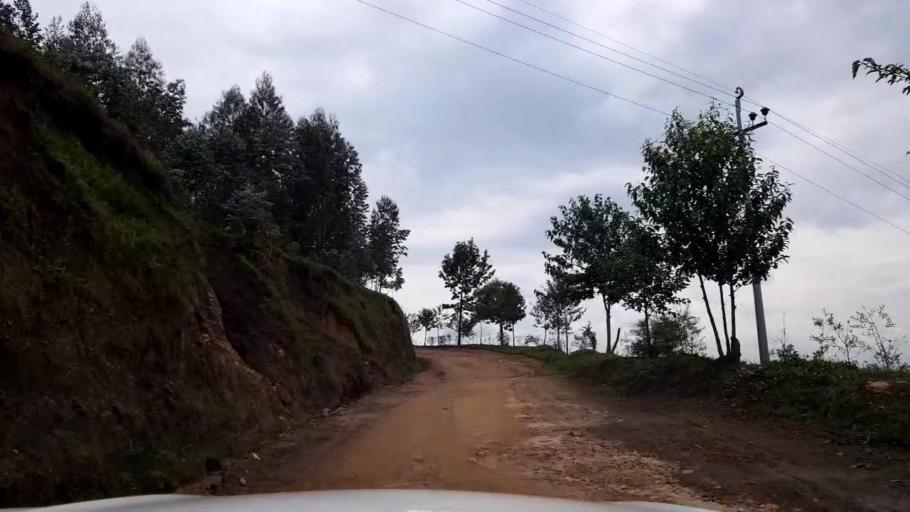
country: RW
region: Western Province
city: Kibuye
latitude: -1.9587
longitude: 29.4024
